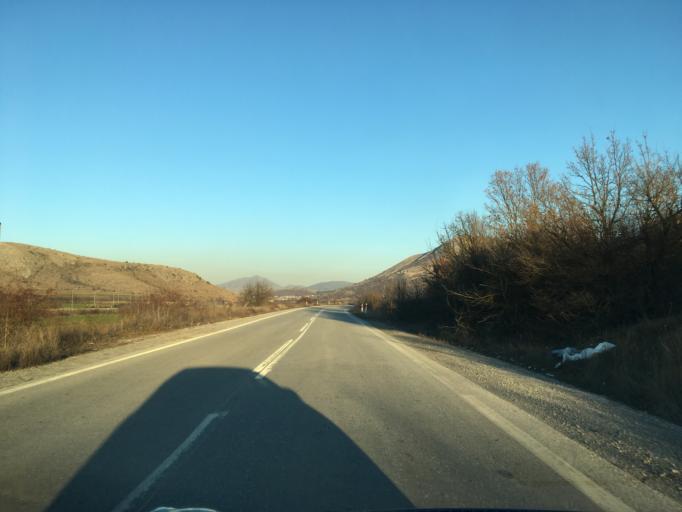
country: GR
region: West Macedonia
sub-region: Nomos Kozanis
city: Kozani
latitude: 40.3173
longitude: 21.7444
